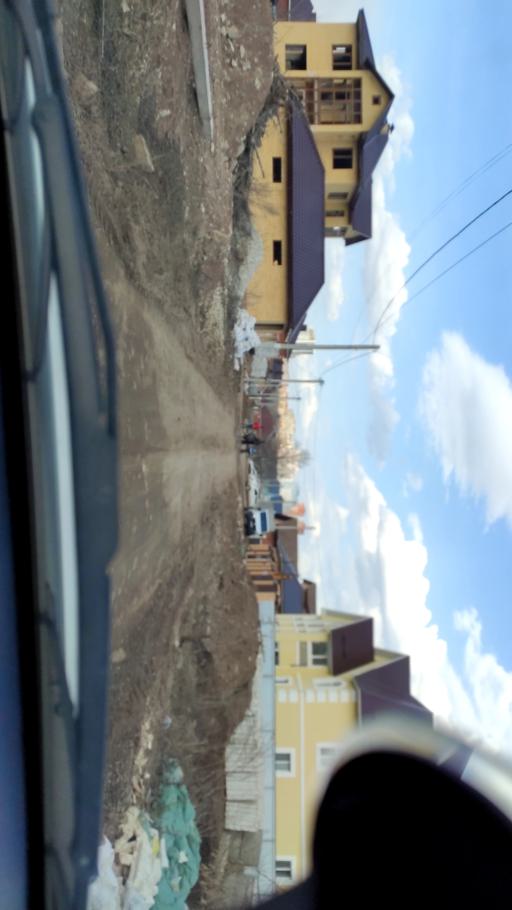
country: RU
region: Bashkortostan
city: Ufa
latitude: 54.6846
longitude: 55.9742
